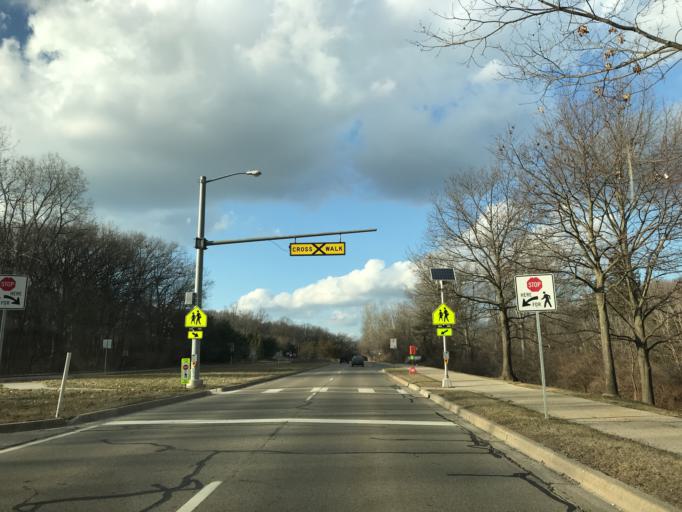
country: US
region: Michigan
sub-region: Washtenaw County
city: Ann Arbor
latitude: 42.2832
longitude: -83.7007
